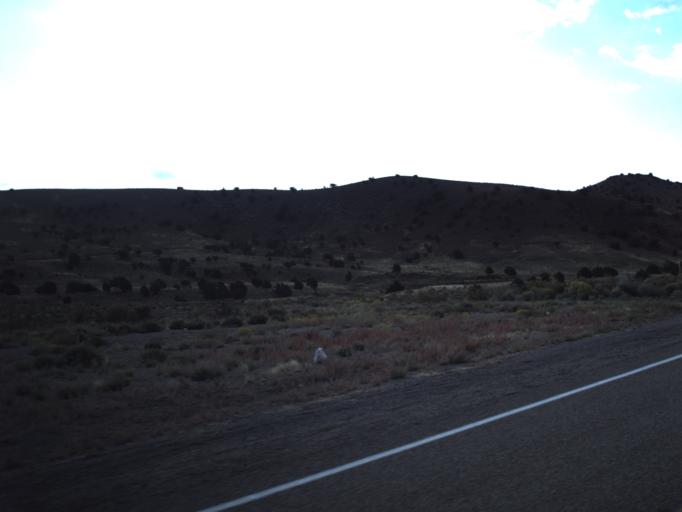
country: US
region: Utah
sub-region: Beaver County
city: Milford
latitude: 38.4533
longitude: -113.2594
